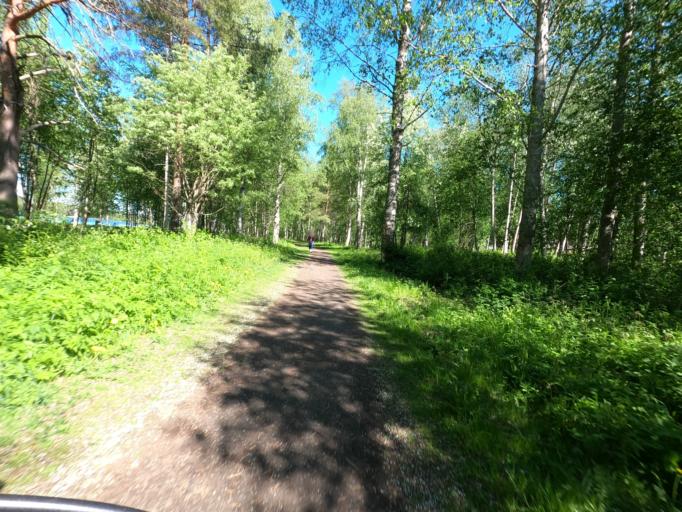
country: FI
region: North Karelia
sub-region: Joensuu
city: Joensuu
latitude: 62.6050
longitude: 29.8132
